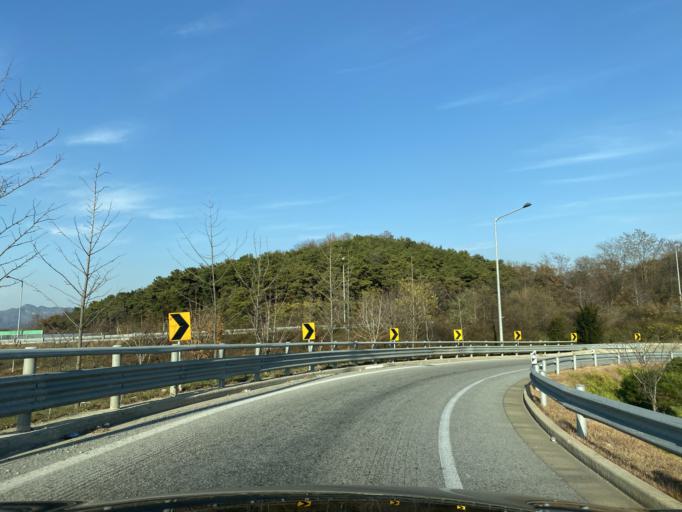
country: KR
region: Chungcheongnam-do
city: Asan
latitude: 36.7809
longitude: 126.9388
